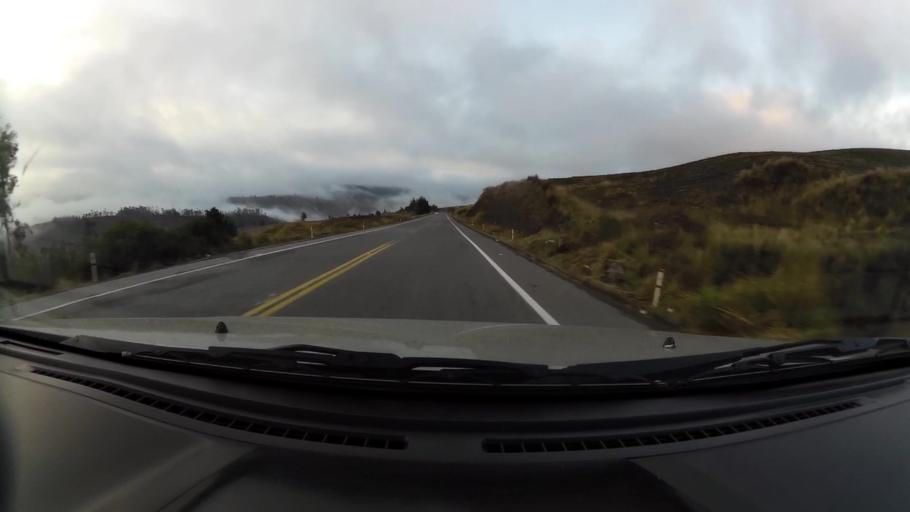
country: EC
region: Chimborazo
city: Alausi
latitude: -2.1051
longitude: -78.7488
